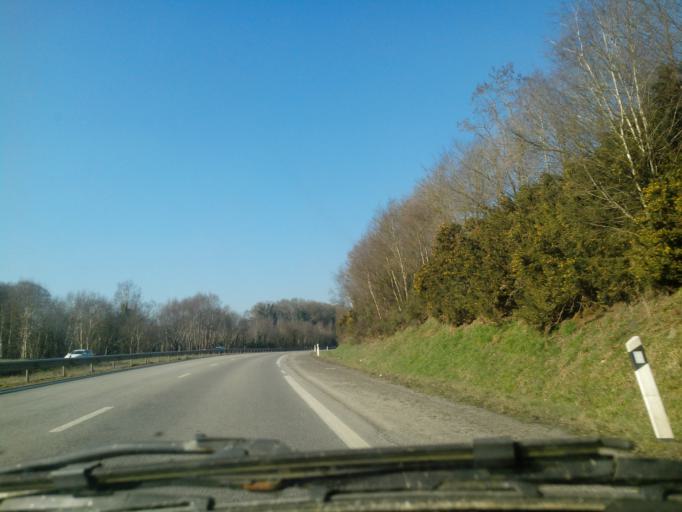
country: FR
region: Brittany
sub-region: Departement des Cotes-d'Armor
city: Plemet
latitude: 48.1689
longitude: -2.6469
